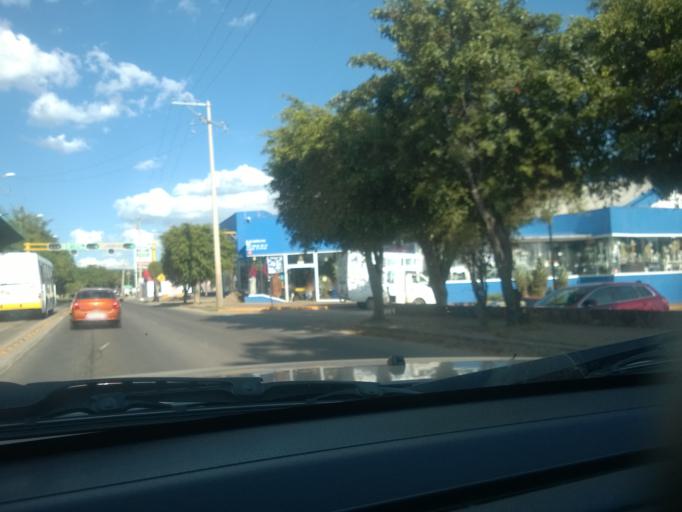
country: MX
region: Guanajuato
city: Leon
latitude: 21.1476
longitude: -101.6775
